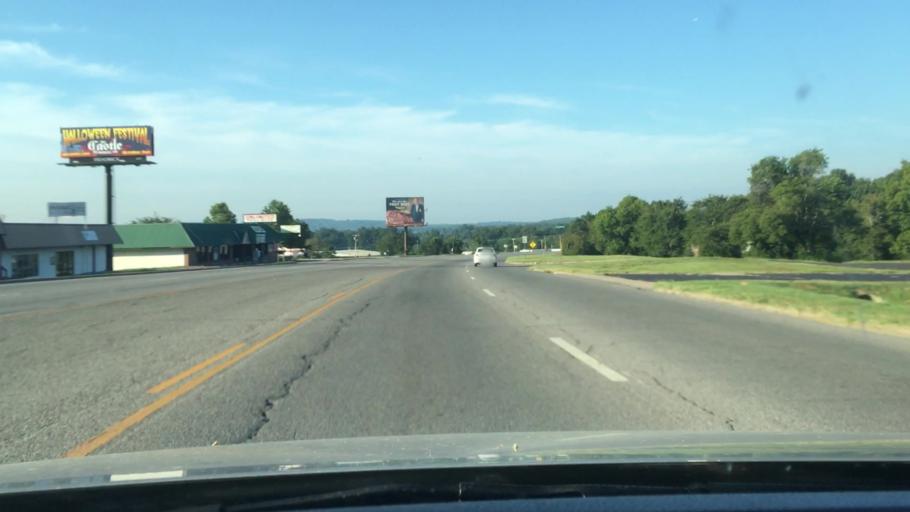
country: US
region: Oklahoma
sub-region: Cherokee County
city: Park Hill
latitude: 35.8617
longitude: -94.9770
